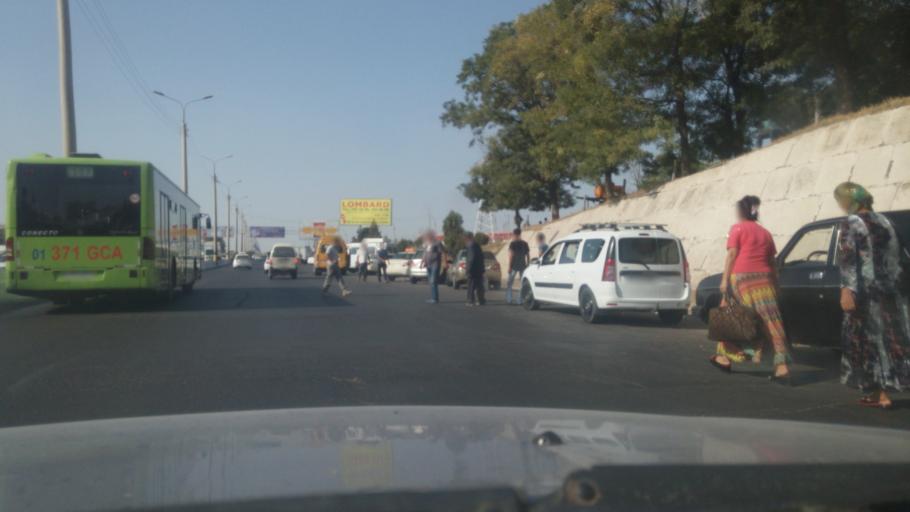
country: UZ
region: Toshkent Shahri
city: Tashkent
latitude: 41.2390
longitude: 69.1677
